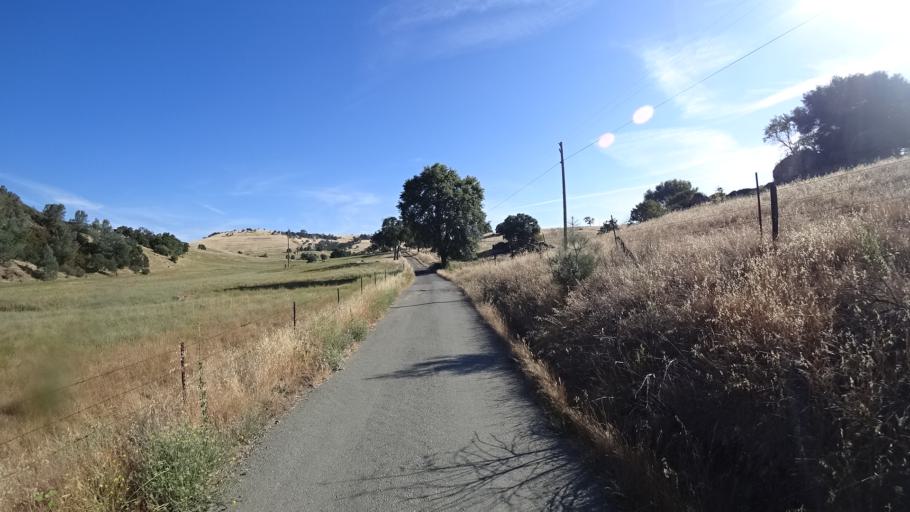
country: US
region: California
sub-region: Calaveras County
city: Valley Springs
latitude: 38.2163
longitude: -120.7858
